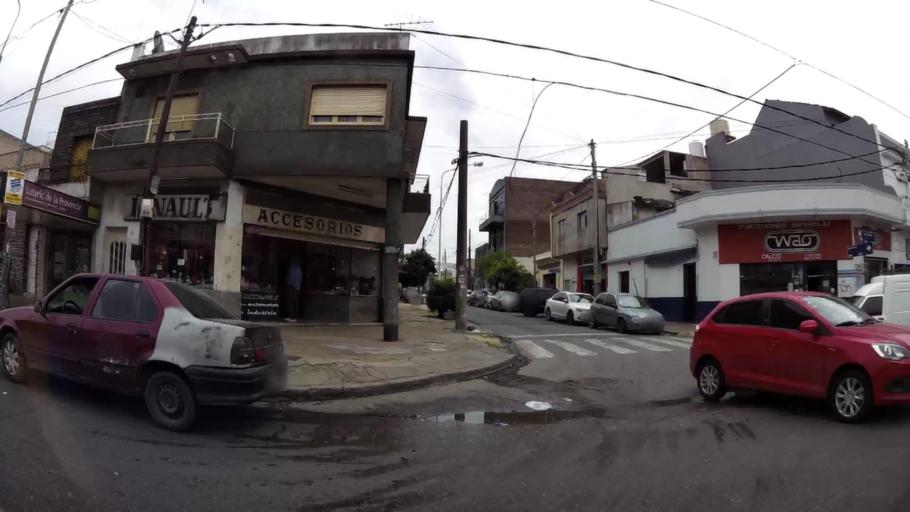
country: AR
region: Buenos Aires F.D.
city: Villa Lugano
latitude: -34.6775
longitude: -58.5074
